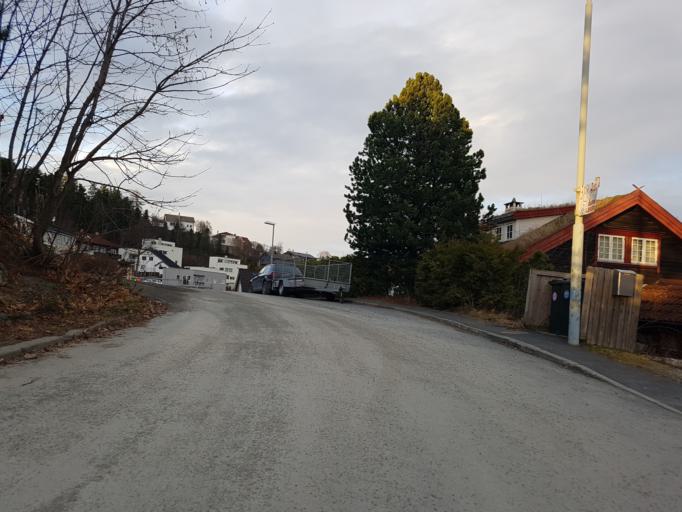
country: NO
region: Sor-Trondelag
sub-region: Trondheim
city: Trondheim
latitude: 63.4184
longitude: 10.3715
